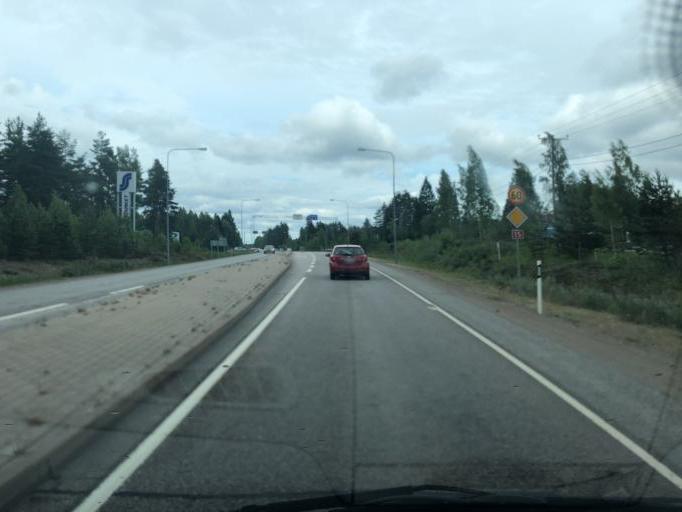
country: FI
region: Kymenlaakso
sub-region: Kouvola
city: Kouvola
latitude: 60.9116
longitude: 26.7654
